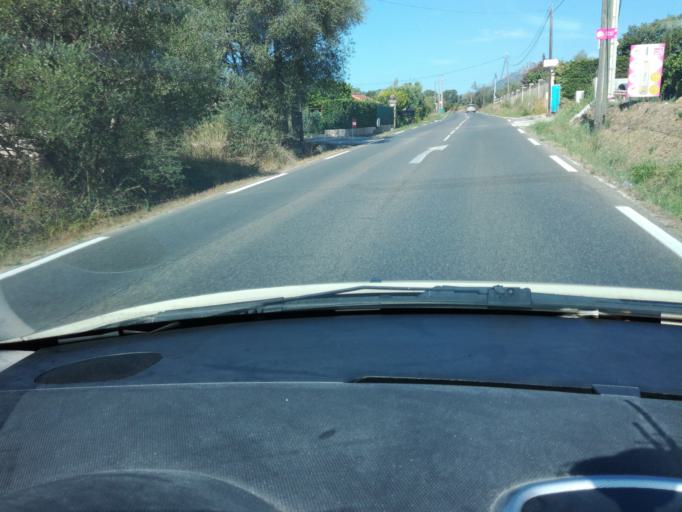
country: FR
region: Provence-Alpes-Cote d'Azur
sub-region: Departement du Var
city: La Crau
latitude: 43.1281
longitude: 6.0942
